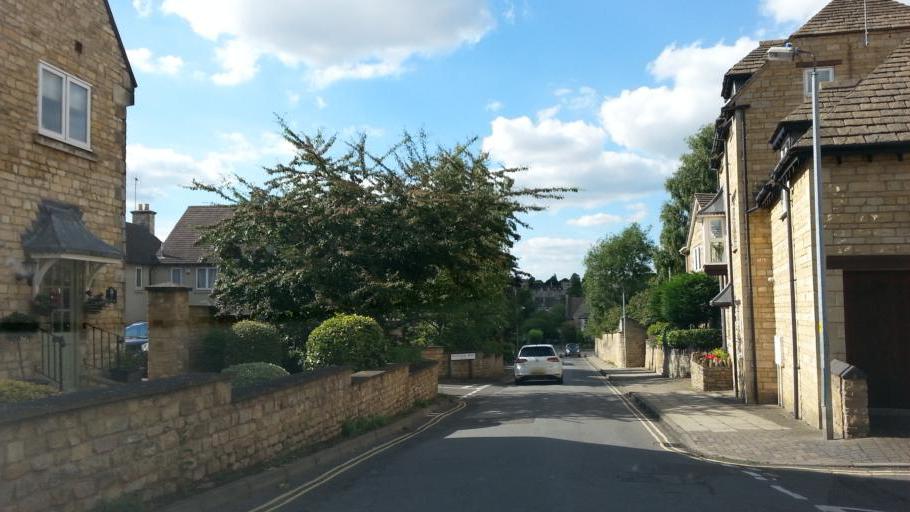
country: GB
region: England
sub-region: Lincolnshire
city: Stamford
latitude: 52.6485
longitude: -0.4791
